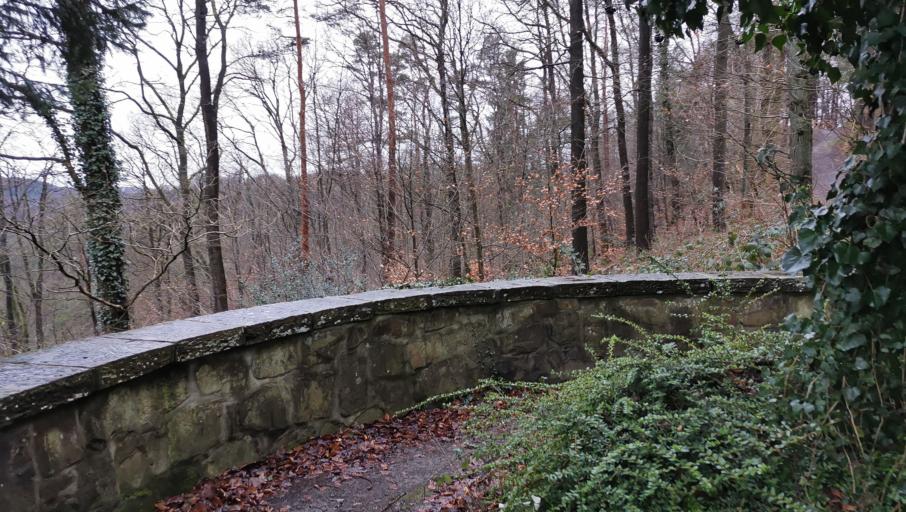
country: DE
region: North Rhine-Westphalia
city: Burscheid
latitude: 51.1415
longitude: 7.1272
